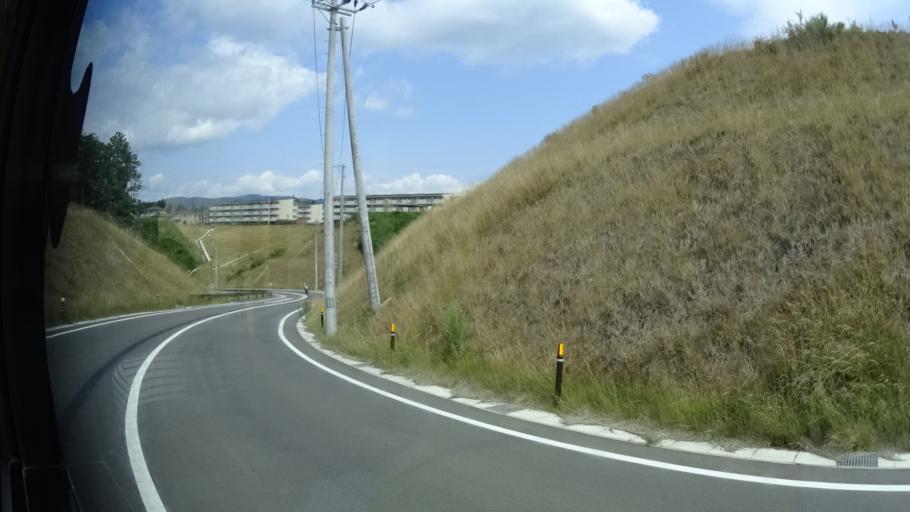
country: JP
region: Miyagi
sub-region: Oshika Gun
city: Onagawa Cho
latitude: 38.6789
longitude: 141.4598
